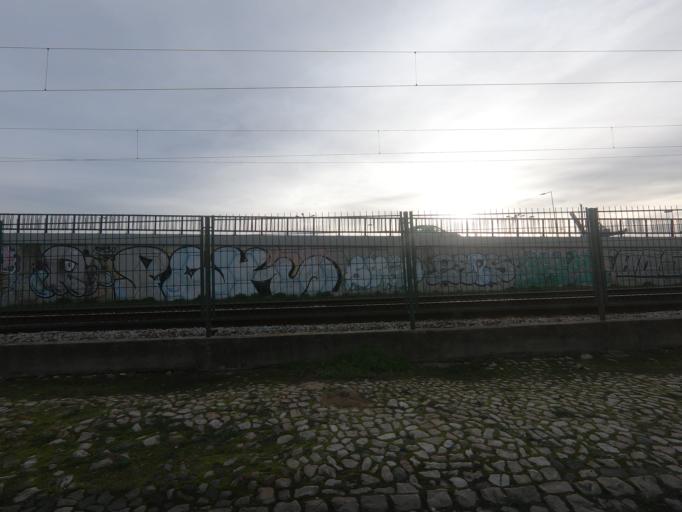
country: PT
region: Setubal
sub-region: Setubal
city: Setubal
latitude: 38.5151
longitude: -8.8659
